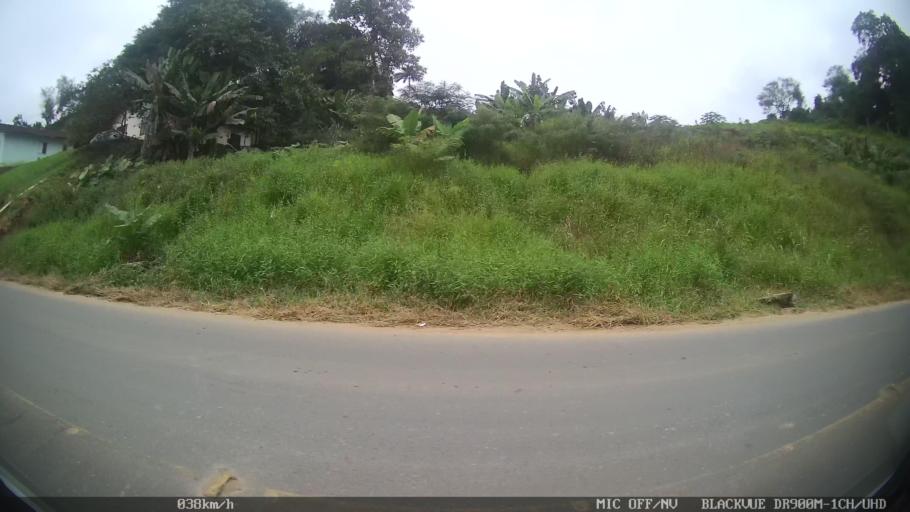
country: BR
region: Santa Catarina
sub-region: Joinville
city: Joinville
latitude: -26.3495
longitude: -48.8240
